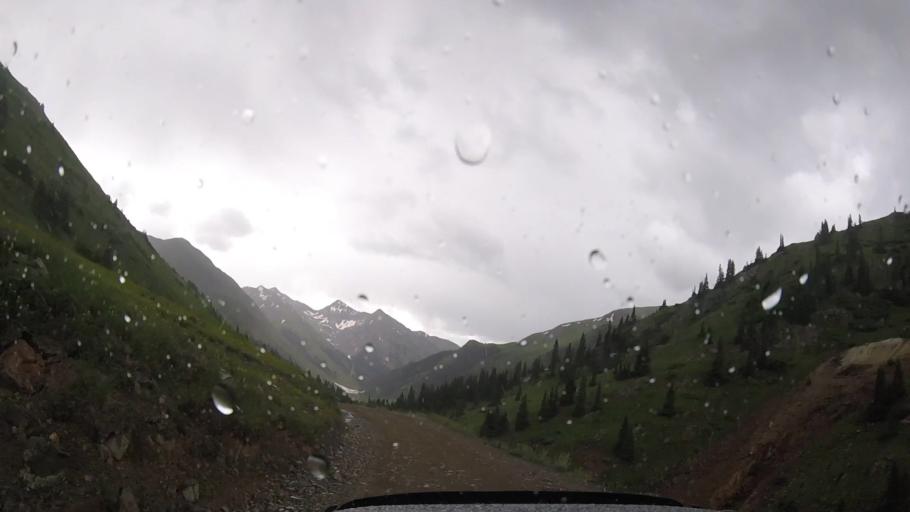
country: US
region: Colorado
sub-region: Ouray County
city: Ouray
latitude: 37.9377
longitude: -107.5724
